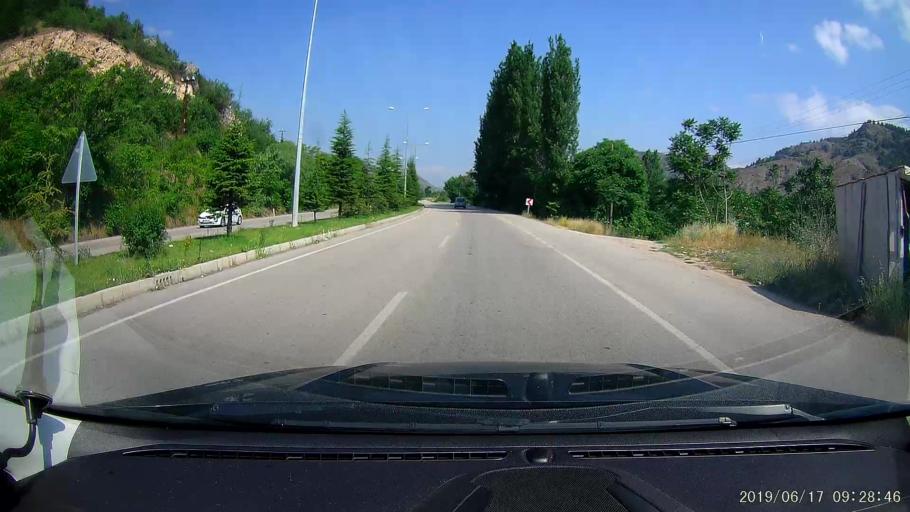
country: TR
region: Amasya
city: Amasya
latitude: 40.6919
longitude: 35.8205
